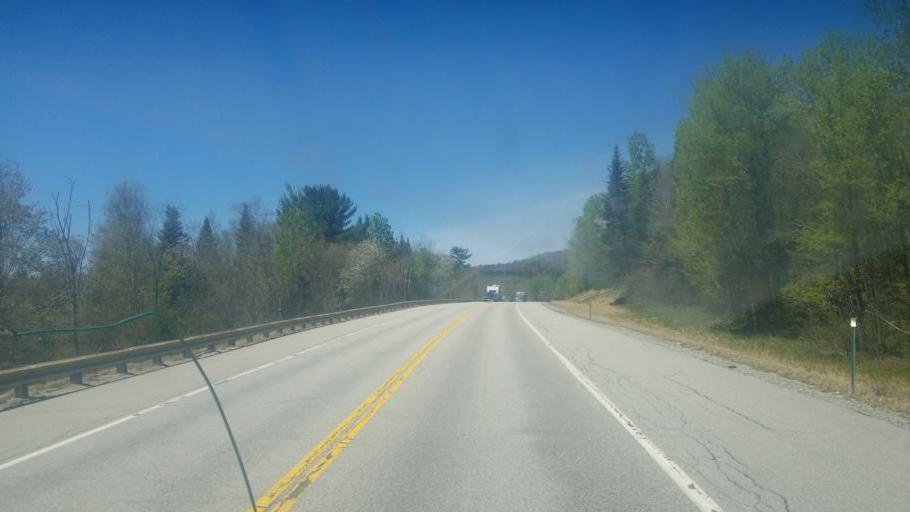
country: US
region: New Hampshire
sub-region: Grafton County
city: Deerfield
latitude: 44.2701
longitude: -71.5099
